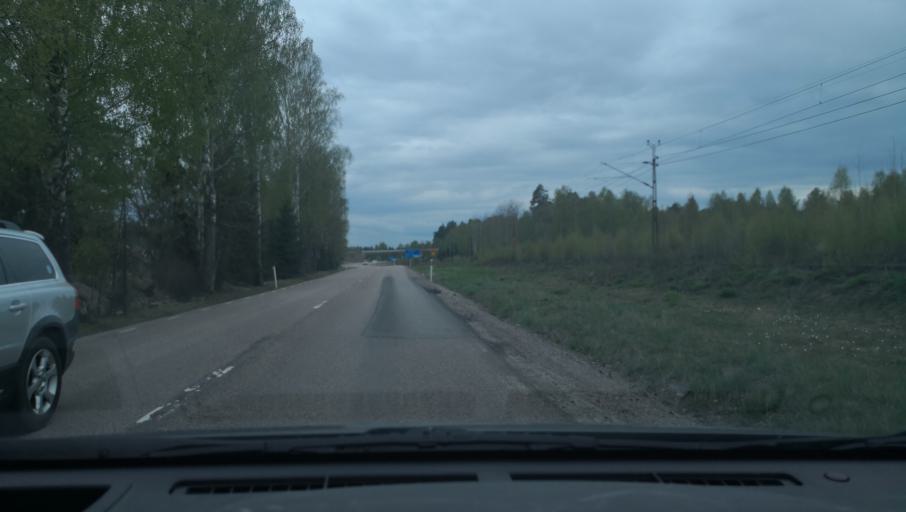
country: SE
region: Dalarna
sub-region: Avesta Kommun
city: Avesta
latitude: 60.1487
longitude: 16.2350
